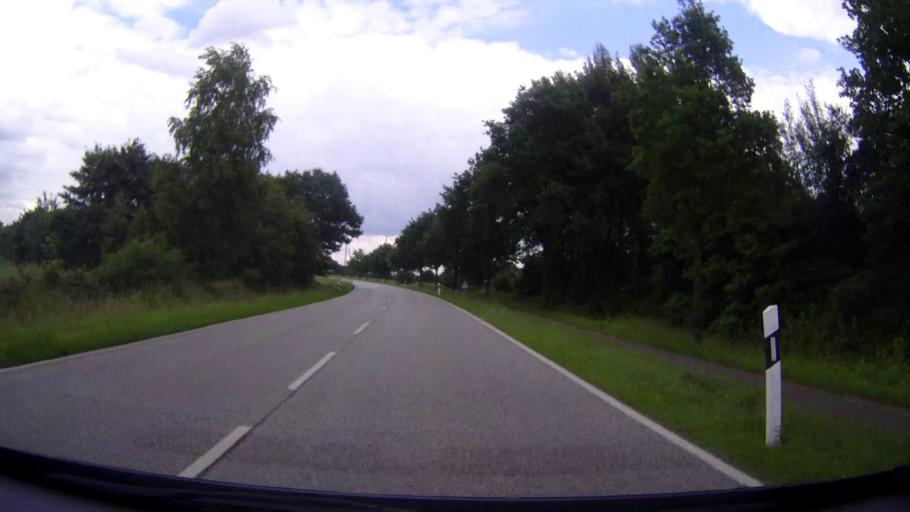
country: DE
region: Schleswig-Holstein
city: Beldorf
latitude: 54.1207
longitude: 9.3460
